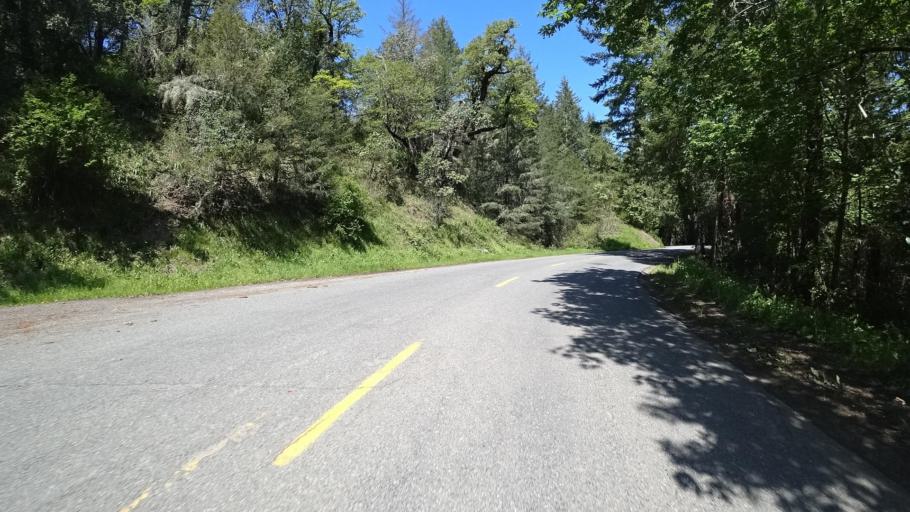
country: US
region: California
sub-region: Humboldt County
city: Redway
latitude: 40.1350
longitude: -123.6288
